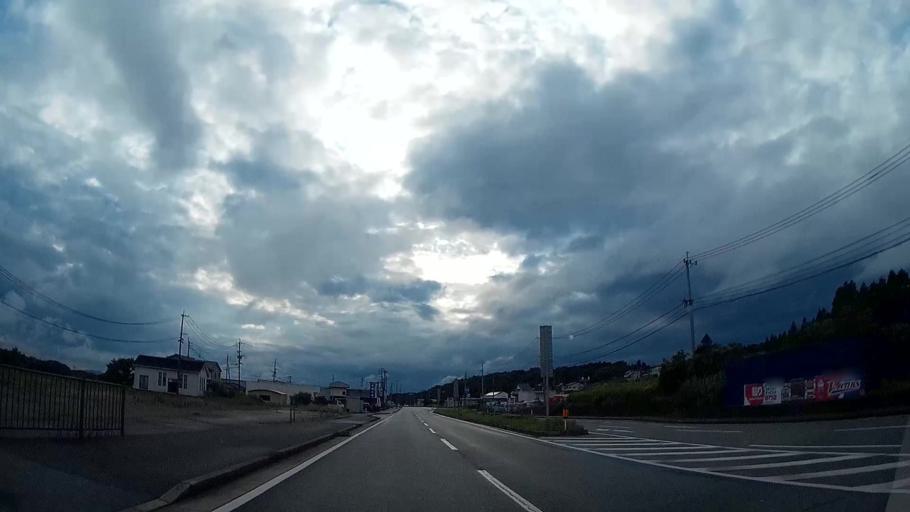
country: JP
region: Kumamoto
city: Ozu
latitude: 32.8798
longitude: 130.9032
